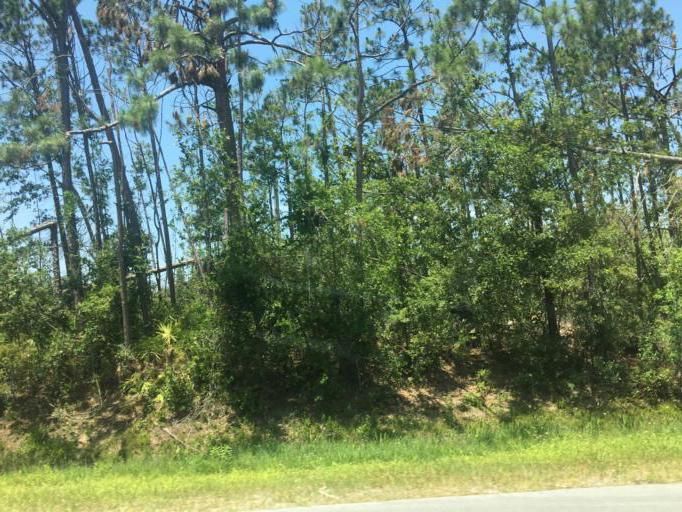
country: US
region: Florida
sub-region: Bay County
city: Pretty Bayou
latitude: 30.2116
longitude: -85.6664
